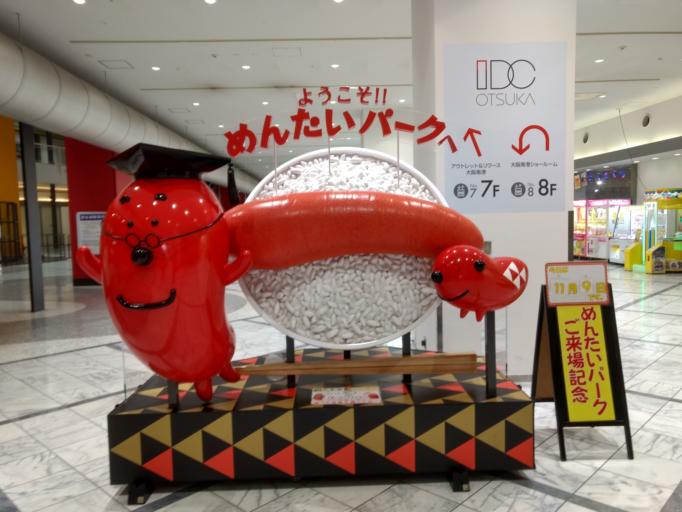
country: JP
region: Osaka
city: Sakai
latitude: 34.6381
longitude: 135.4112
